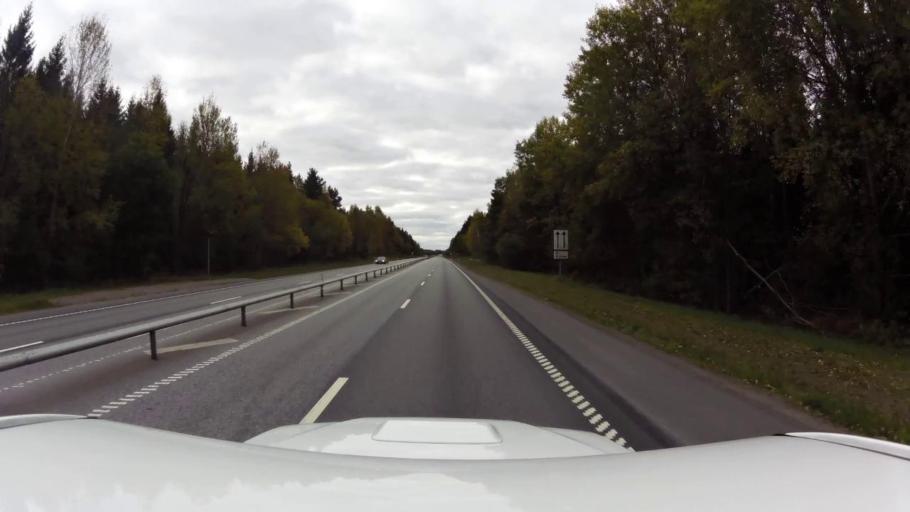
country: SE
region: OEstergoetland
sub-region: Linkopings Kommun
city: Malmslatt
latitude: 58.3784
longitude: 15.5425
